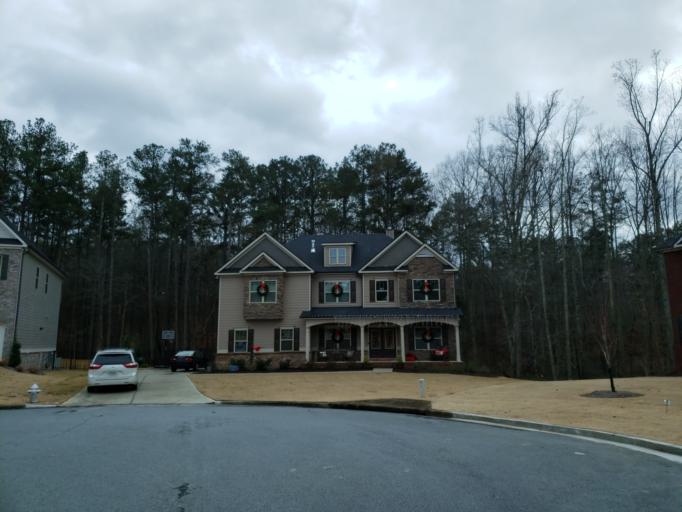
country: US
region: Georgia
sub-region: Cobb County
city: Fair Oaks
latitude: 33.9174
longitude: -84.5983
